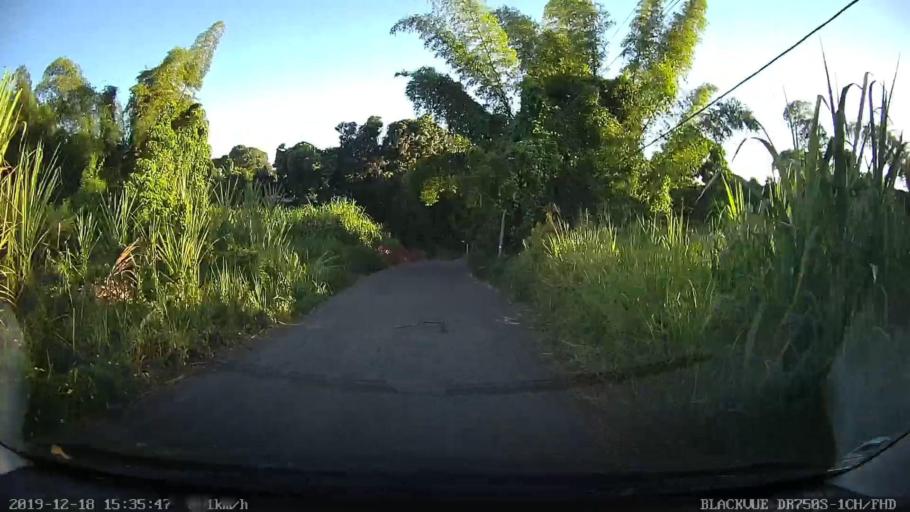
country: RE
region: Reunion
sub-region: Reunion
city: Bras-Panon
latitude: -20.9966
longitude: 55.6630
